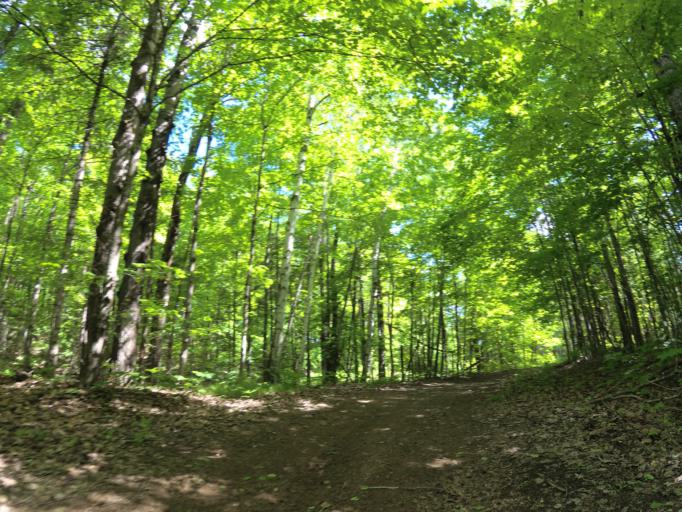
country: CA
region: Ontario
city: Renfrew
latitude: 45.0451
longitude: -76.8262
